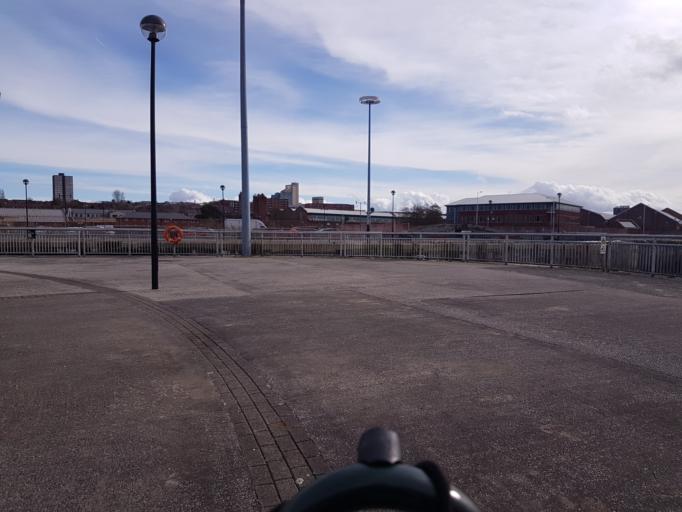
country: GB
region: England
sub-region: Liverpool
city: Liverpool
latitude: 53.3866
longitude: -2.9848
